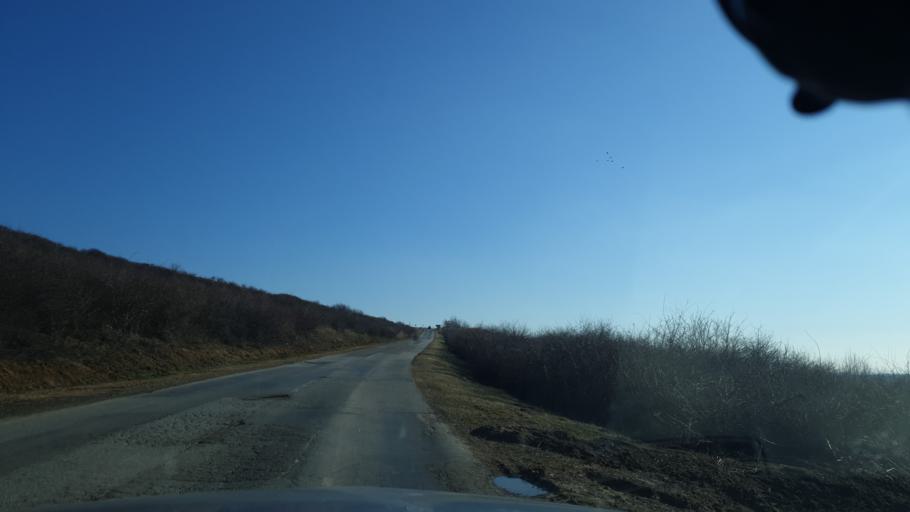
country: RS
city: Vrdnik
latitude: 45.1019
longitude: 19.8033
